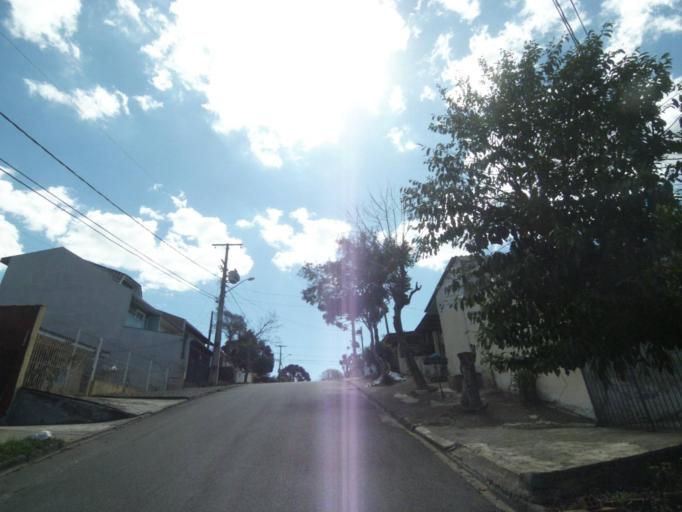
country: BR
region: Parana
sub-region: Curitiba
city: Curitiba
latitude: -25.3828
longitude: -49.2416
